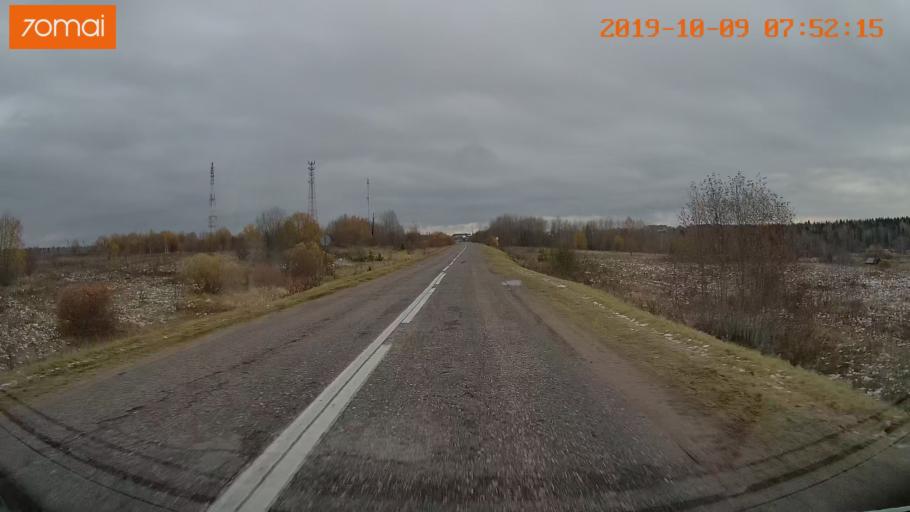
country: RU
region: Jaroslavl
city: Kukoboy
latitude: 58.6899
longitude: 39.8841
